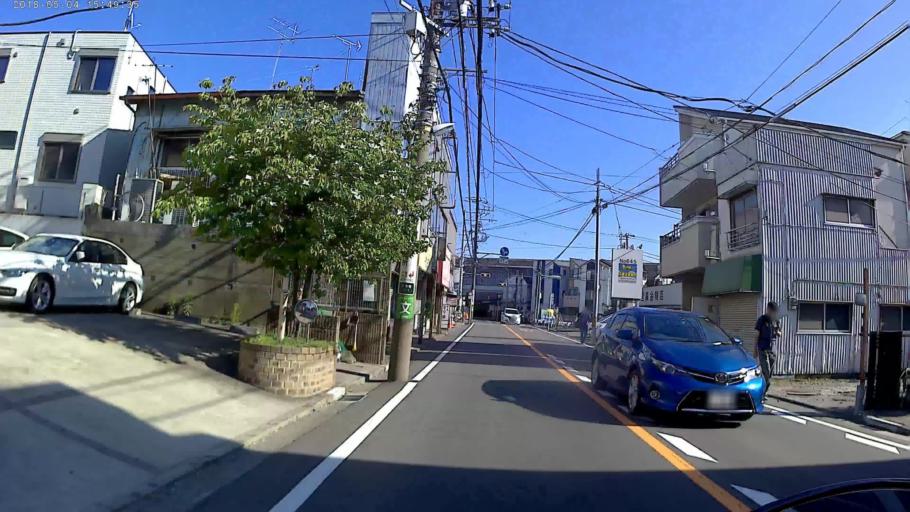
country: JP
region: Kanagawa
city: Yokohama
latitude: 35.4968
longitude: 139.6465
